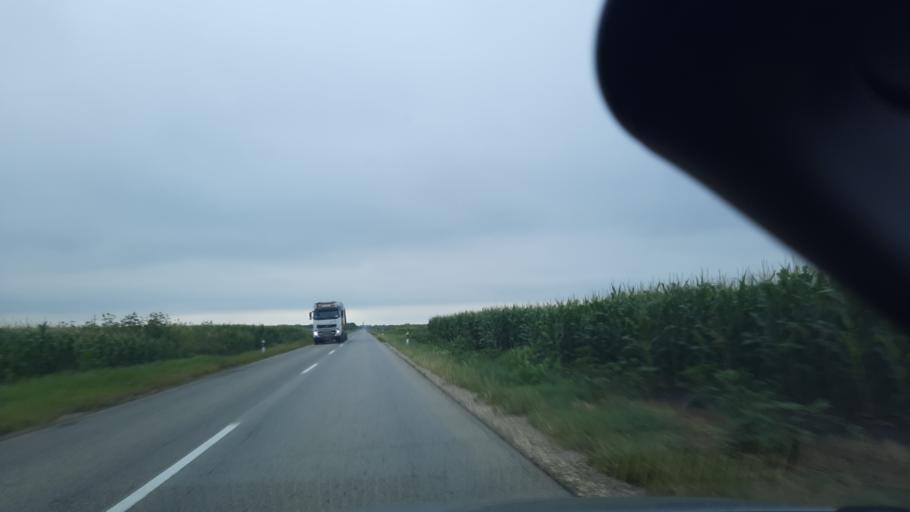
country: RS
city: Farkazdin
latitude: 45.2003
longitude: 20.4375
